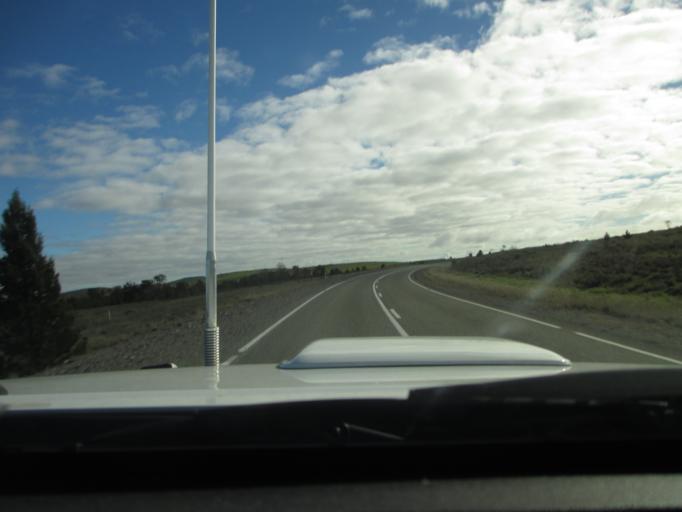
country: AU
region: South Australia
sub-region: Peterborough
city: Peterborough
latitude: -32.5882
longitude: 138.5601
